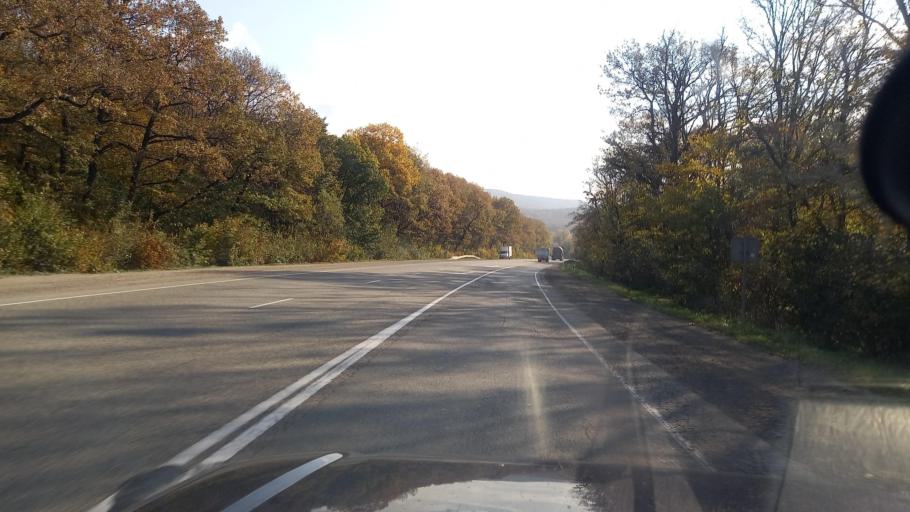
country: RU
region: Krasnodarskiy
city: Verkhnebakanskiy
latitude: 44.8426
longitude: 37.7008
